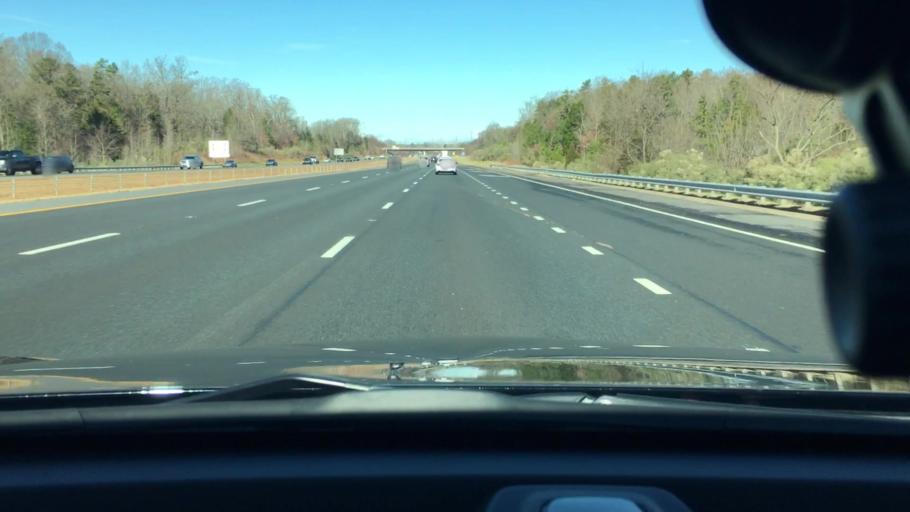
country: US
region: North Carolina
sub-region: Cabarrus County
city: Harrisburg
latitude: 35.2891
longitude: -80.6783
